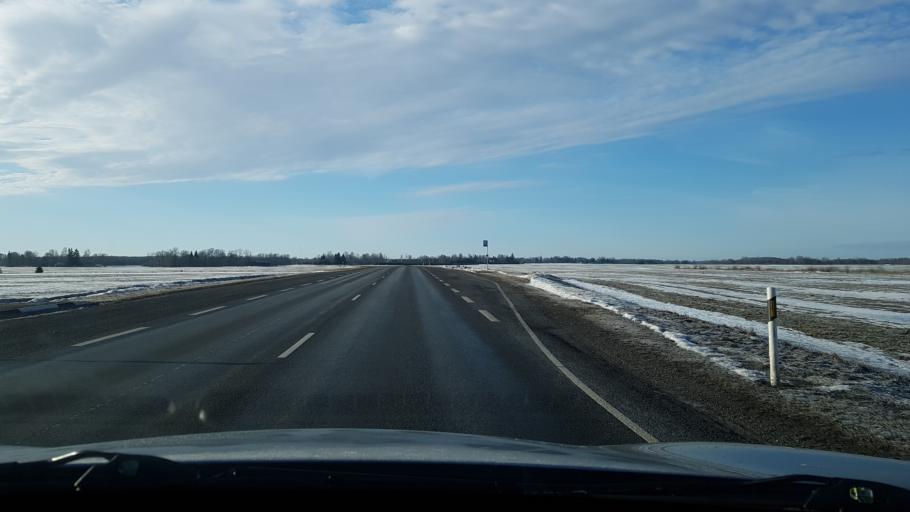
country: EE
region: Viljandimaa
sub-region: Vohma linn
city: Vohma
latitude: 58.6493
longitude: 25.5865
